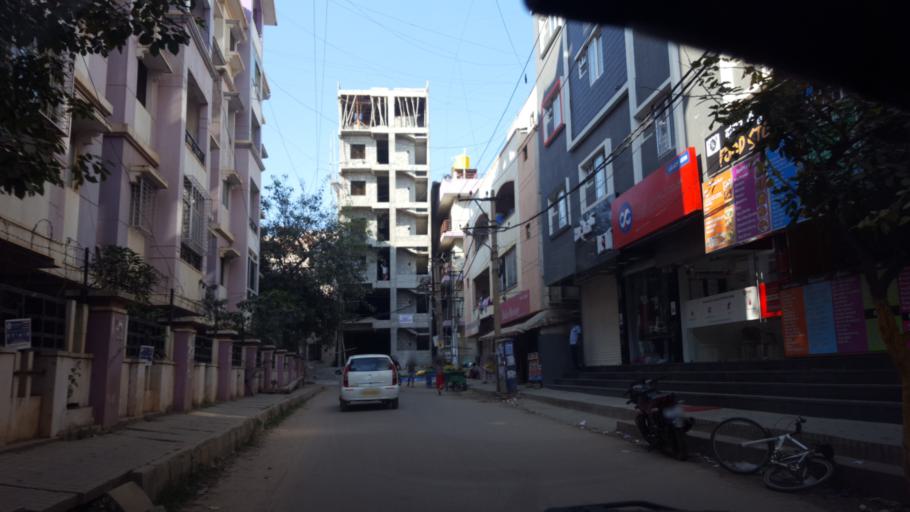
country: IN
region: Karnataka
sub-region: Bangalore Urban
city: Bangalore
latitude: 12.9539
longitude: 77.7150
